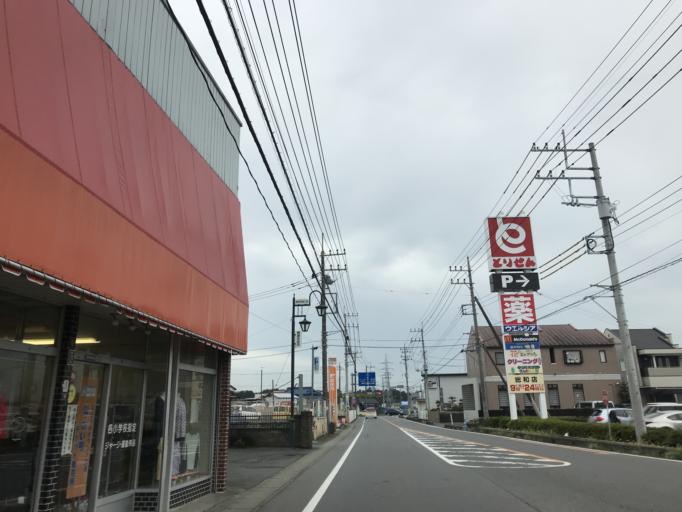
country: JP
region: Ibaraki
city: Koga
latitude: 36.1679
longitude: 139.7685
